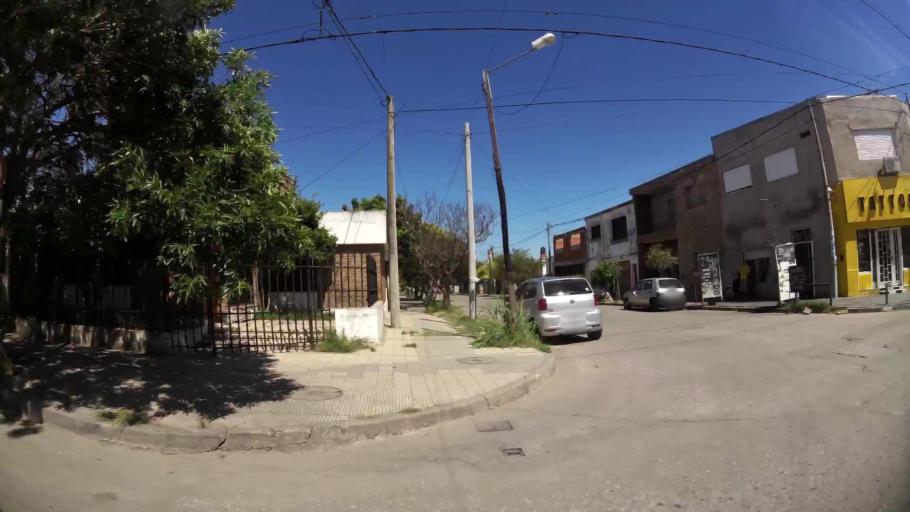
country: AR
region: Cordoba
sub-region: Departamento de Capital
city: Cordoba
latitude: -31.4199
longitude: -64.1400
